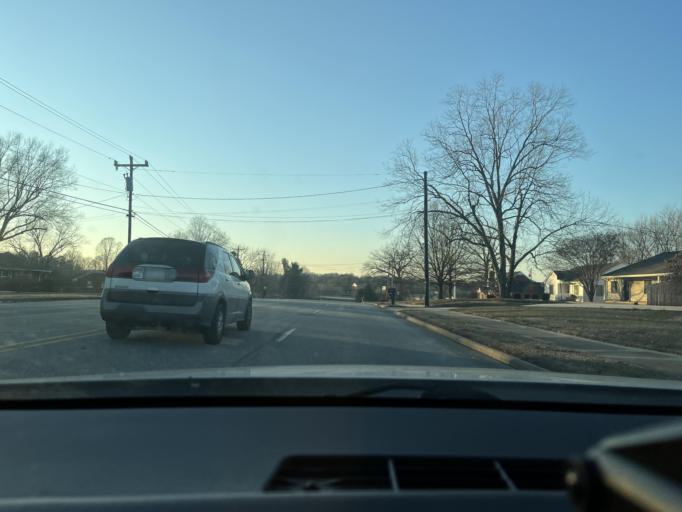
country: US
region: North Carolina
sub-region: Guilford County
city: Greensboro
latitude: 36.0186
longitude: -79.8199
